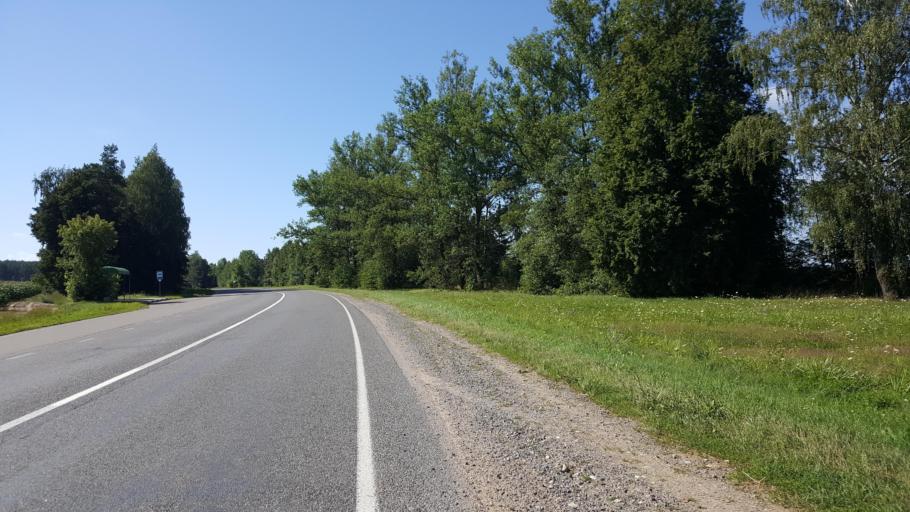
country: BY
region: Brest
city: Kamyanyets
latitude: 52.3566
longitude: 23.7755
